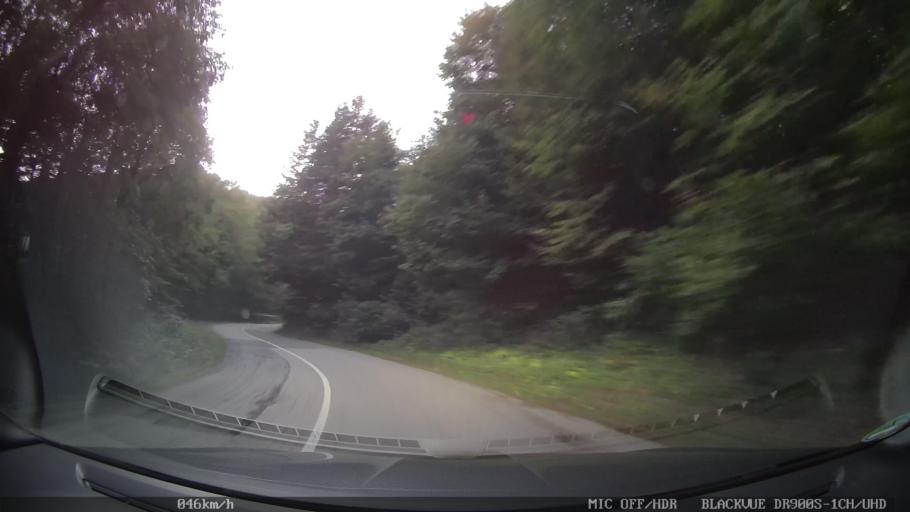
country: HR
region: Primorsko-Goranska
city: Novi Vinodolski
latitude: 45.1983
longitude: 14.8973
